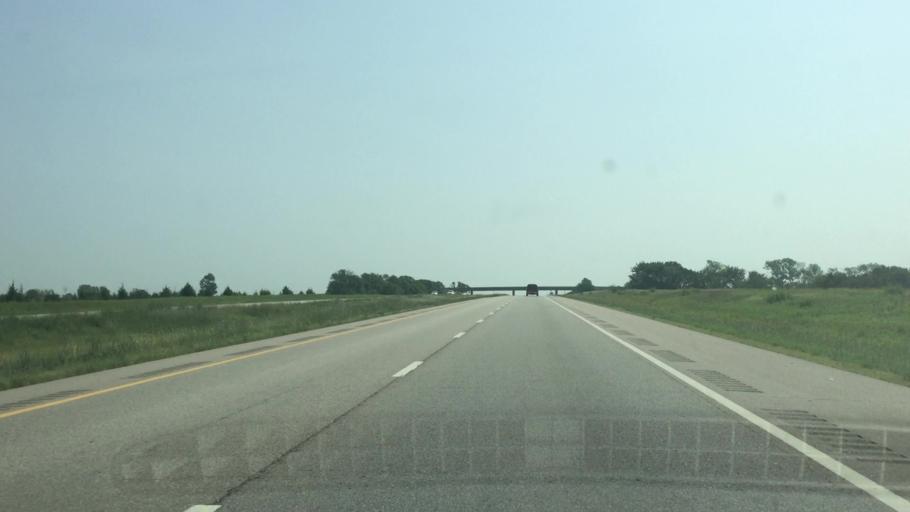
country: US
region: Kansas
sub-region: Lyon County
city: Emporia
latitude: 38.4108
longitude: -95.9574
